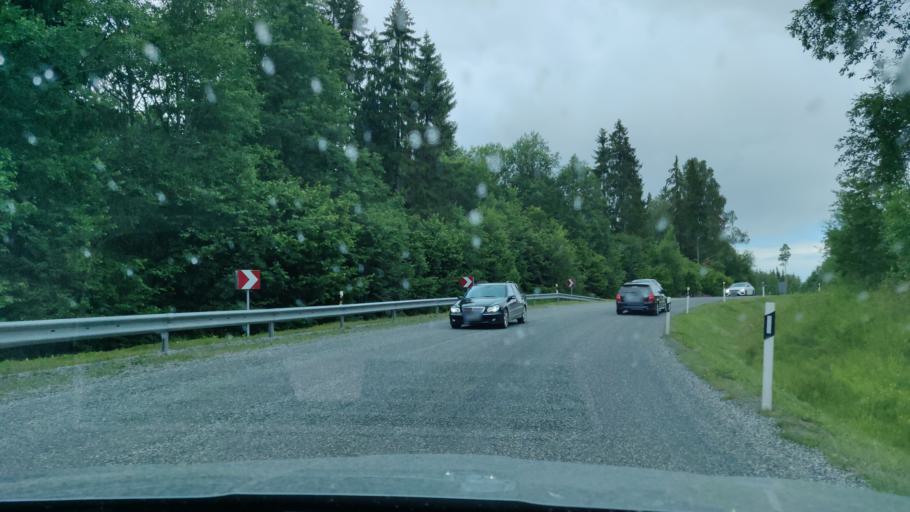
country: EE
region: Vorumaa
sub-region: Antsla vald
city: Vana-Antsla
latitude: 58.0228
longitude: 26.5800
